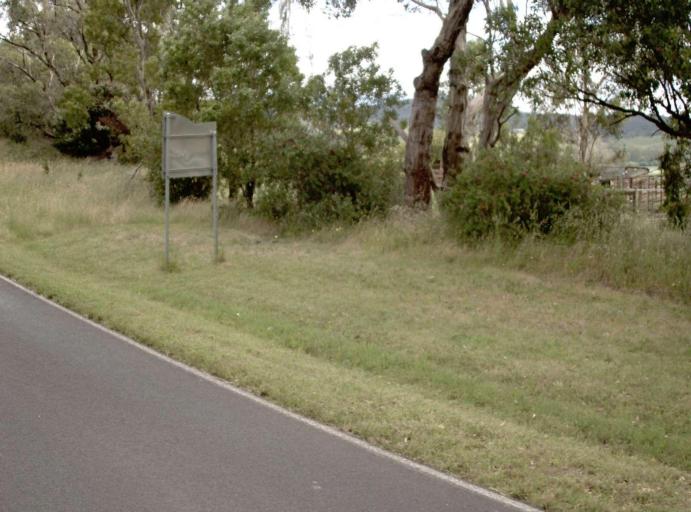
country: AU
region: Victoria
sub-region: Latrobe
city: Moe
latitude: -38.1047
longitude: 146.2382
